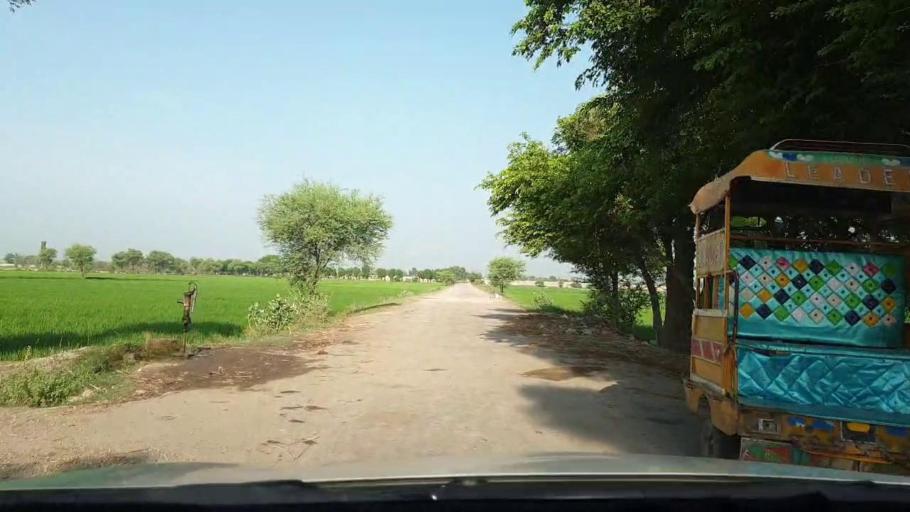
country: PK
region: Sindh
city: Larkana
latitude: 27.5454
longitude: 68.2619
